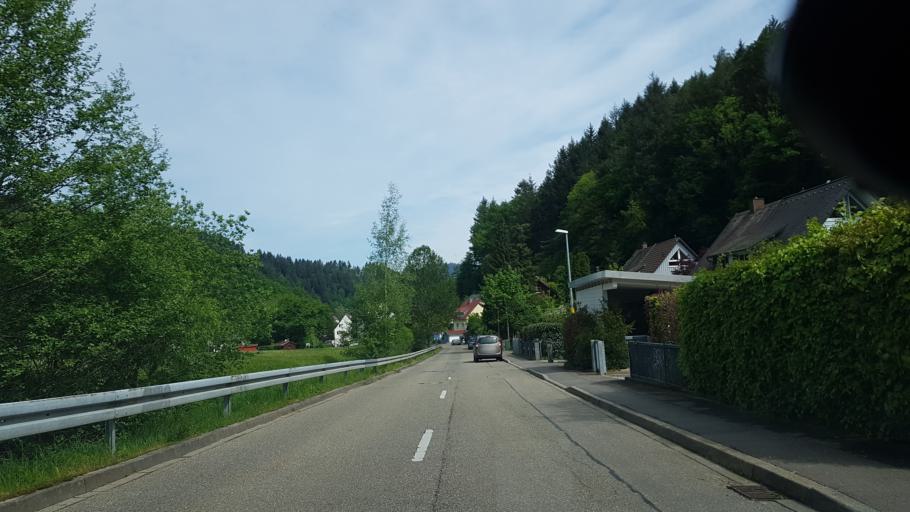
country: DE
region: Baden-Wuerttemberg
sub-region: Freiburg Region
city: Kirchzarten
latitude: 47.9603
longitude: 7.9105
